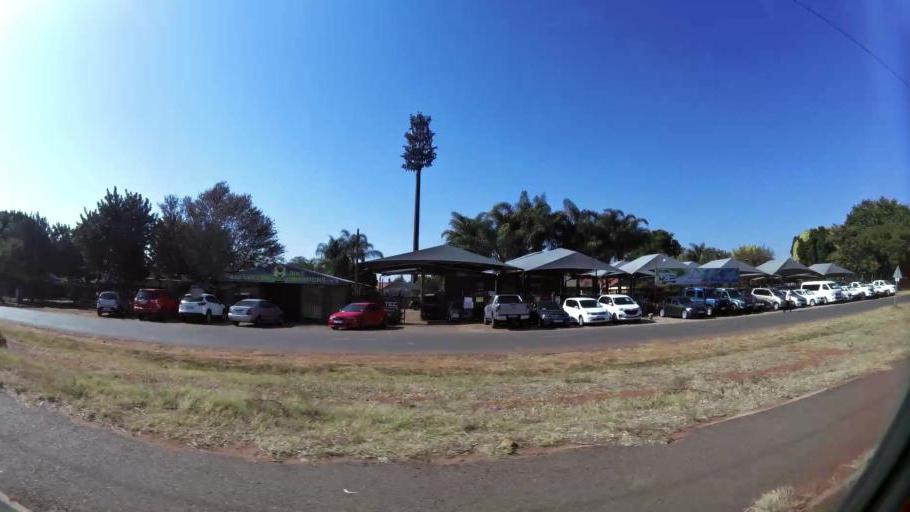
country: ZA
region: North-West
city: Ga-Rankuwa
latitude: -25.6587
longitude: 28.1018
